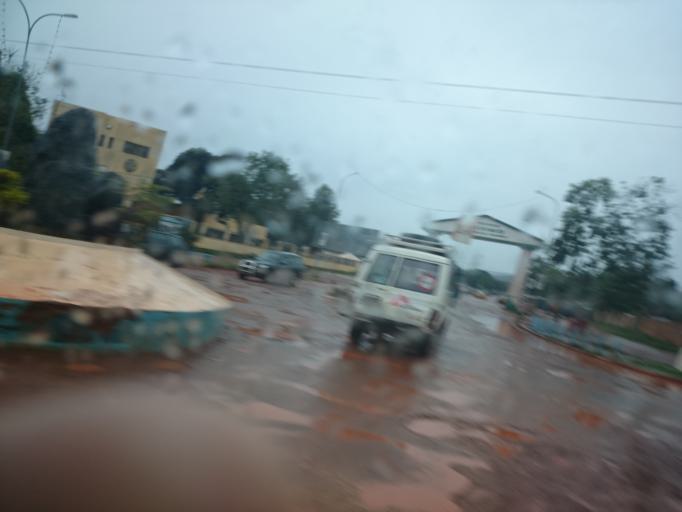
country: CF
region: Bangui
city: Bangui
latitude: 4.3655
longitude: 18.5617
